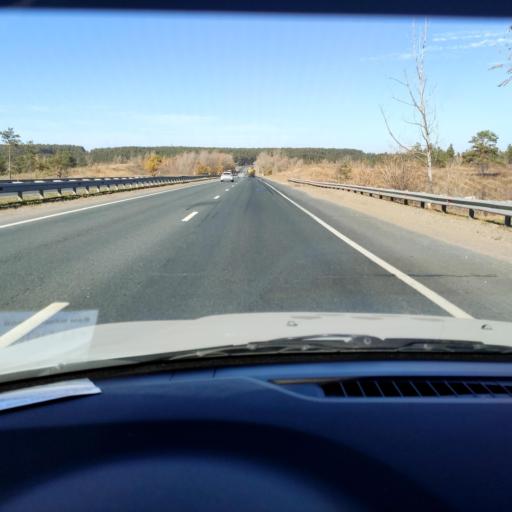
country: RU
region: Samara
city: Zhigulevsk
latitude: 53.5250
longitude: 49.5263
